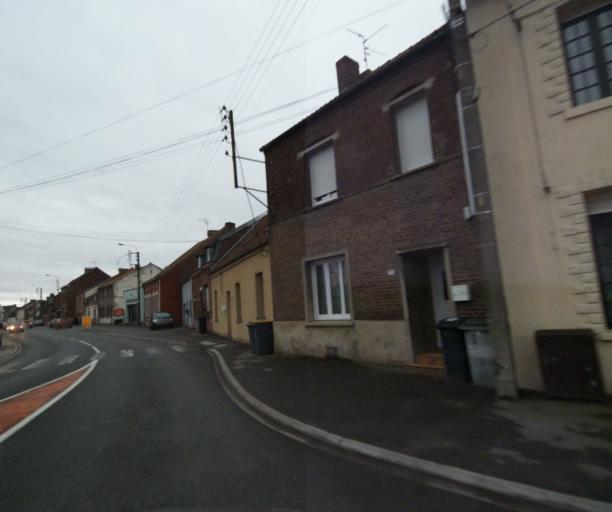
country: FR
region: Nord-Pas-de-Calais
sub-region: Departement du Nord
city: Aubry-du-Hainaut
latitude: 50.3697
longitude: 3.4580
